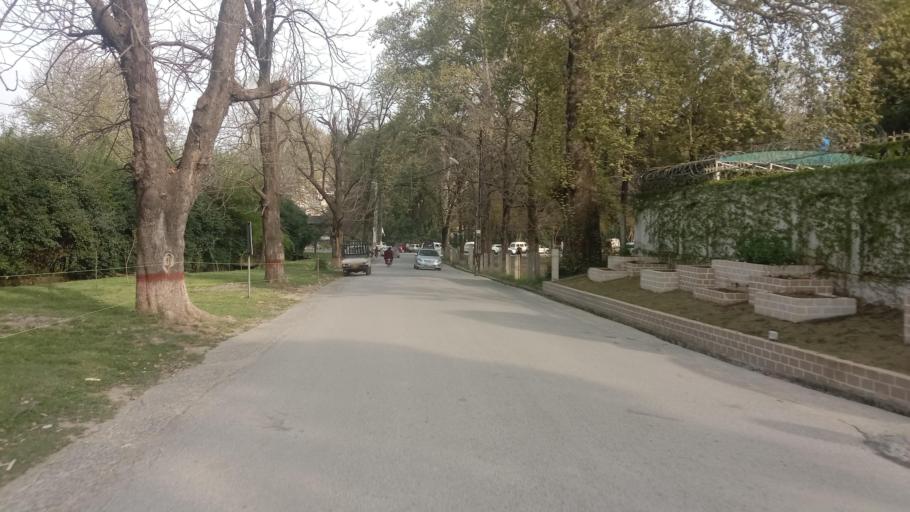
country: PK
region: Khyber Pakhtunkhwa
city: Abbottabad
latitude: 34.1515
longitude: 73.2146
